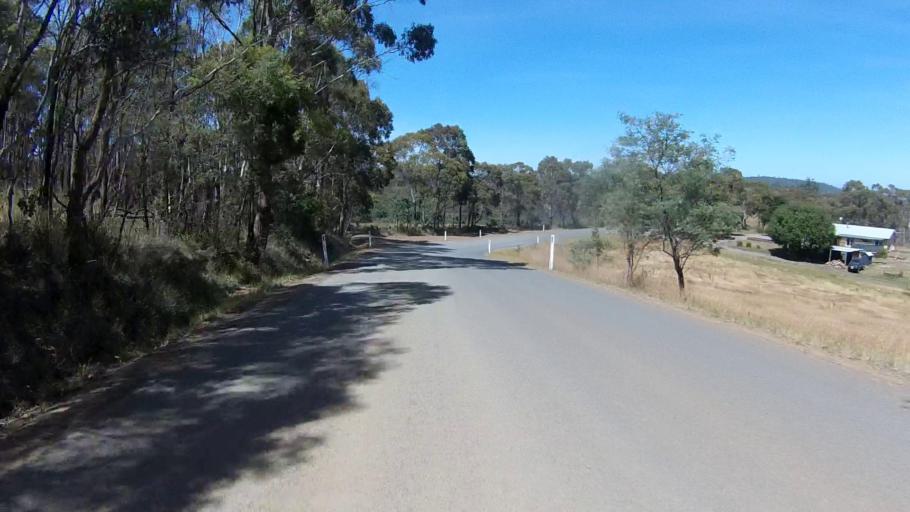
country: AU
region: Tasmania
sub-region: Sorell
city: Sorell
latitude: -42.7463
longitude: 147.7281
